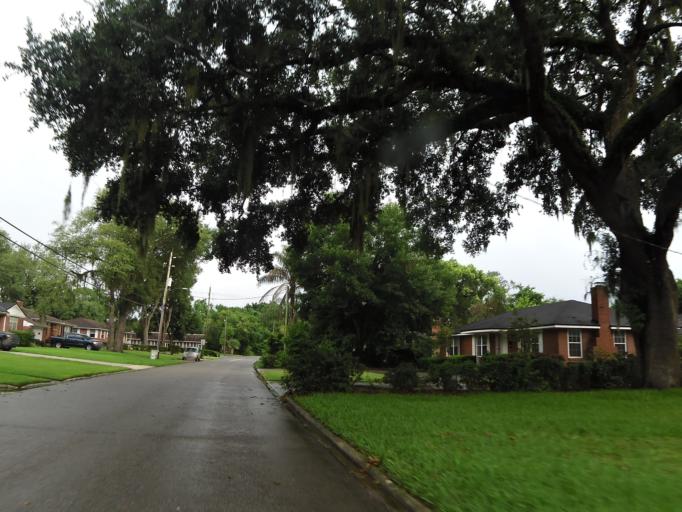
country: US
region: Florida
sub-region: Duval County
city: Jacksonville
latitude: 30.3075
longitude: -81.6255
